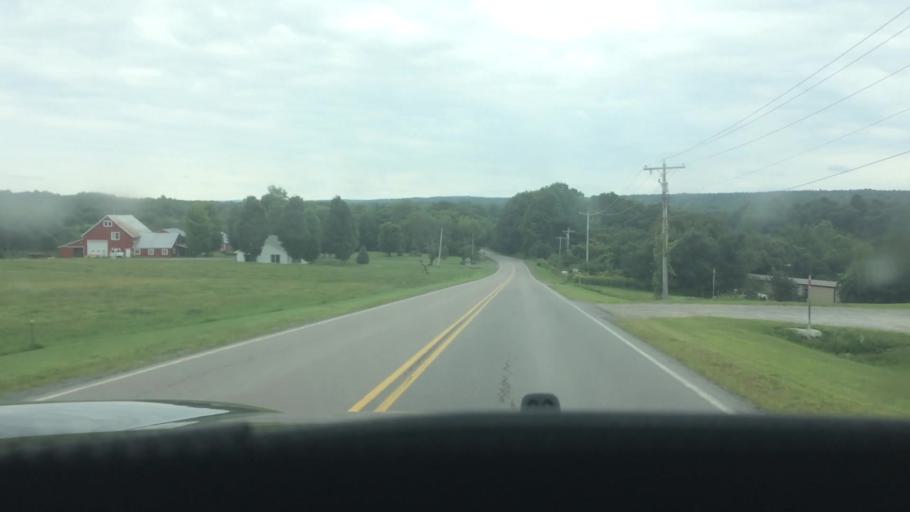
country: US
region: New York
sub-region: St. Lawrence County
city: Canton
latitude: 44.5396
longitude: -75.0784
